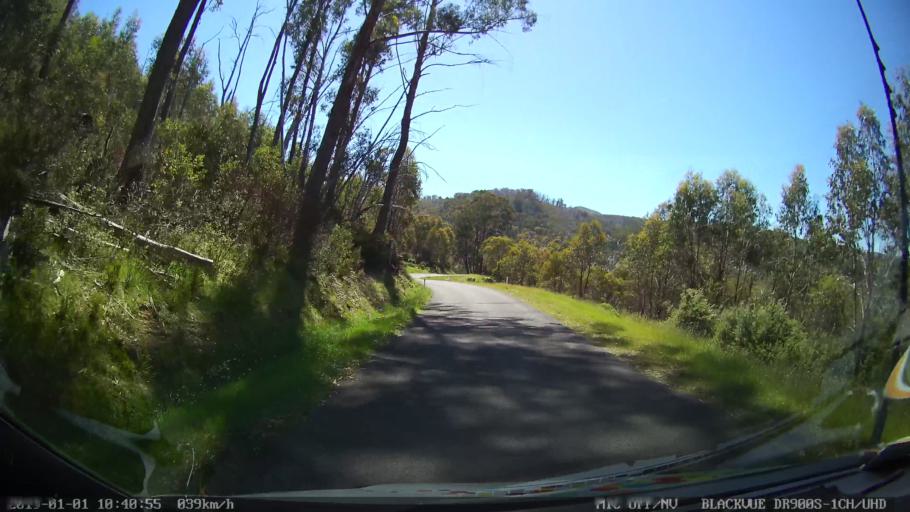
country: AU
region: New South Wales
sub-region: Snowy River
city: Jindabyne
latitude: -36.0370
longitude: 148.3160
